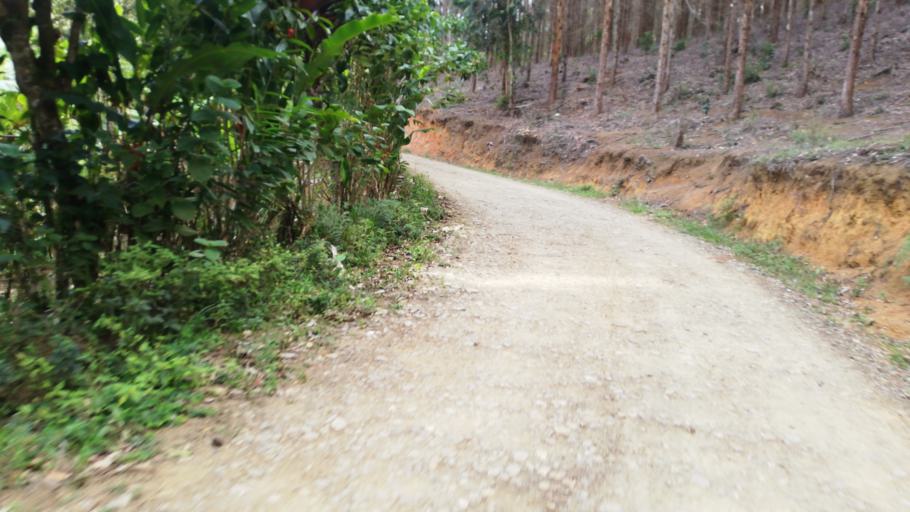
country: CO
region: Valle del Cauca
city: Yumbo
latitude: 3.6319
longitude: -76.5468
